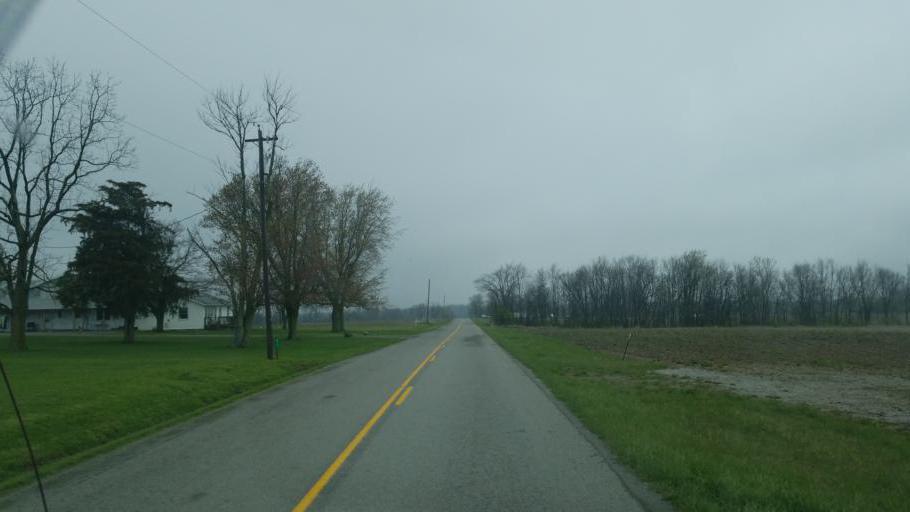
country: US
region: Ohio
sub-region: Logan County
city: Northwood
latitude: 40.4875
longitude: -83.6746
